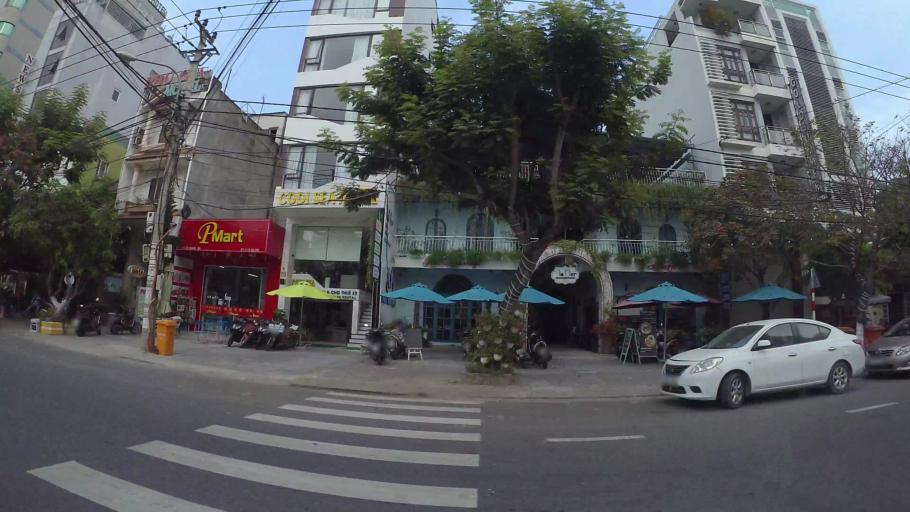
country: VN
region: Da Nang
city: Son Tra
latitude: 16.0671
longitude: 108.2432
